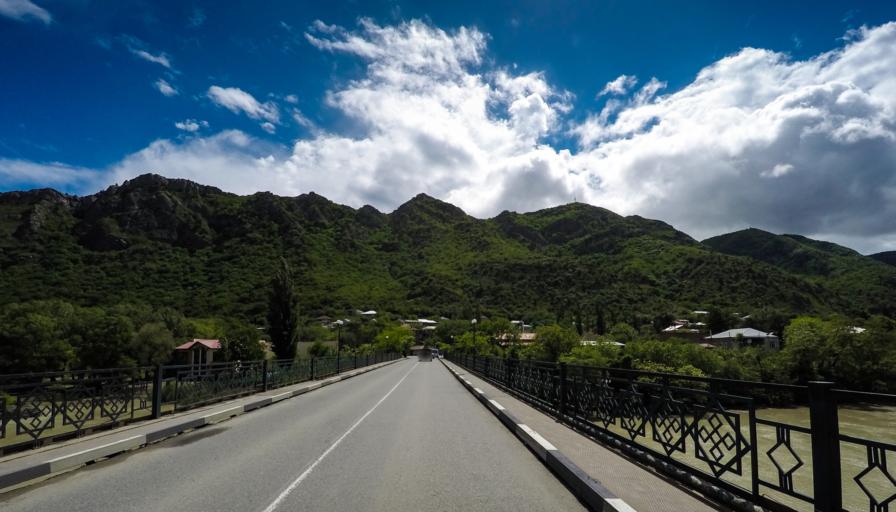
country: GE
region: Mtskheta-Mtianeti
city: Mtskheta
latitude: 41.8396
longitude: 44.7042
